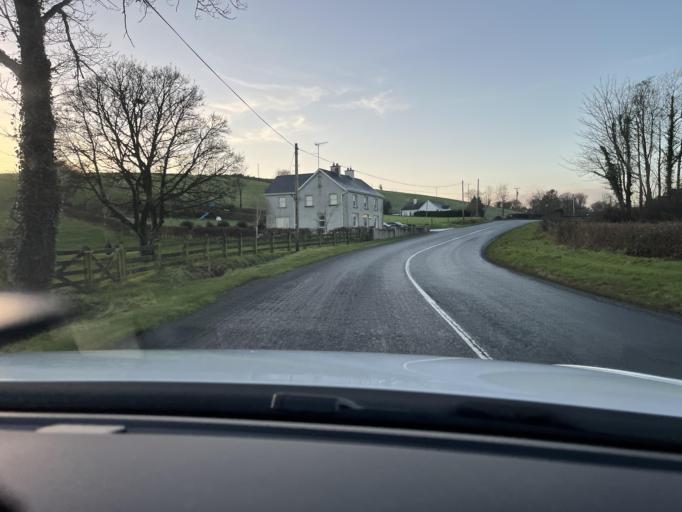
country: IE
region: Ulster
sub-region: An Cabhan
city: Ballyconnell
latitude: 54.0617
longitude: -7.7050
